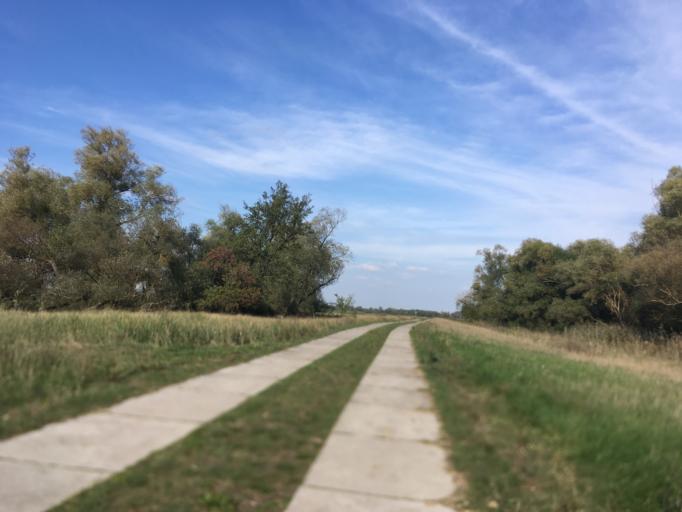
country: DE
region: Brandenburg
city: Schwedt (Oder)
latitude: 53.0234
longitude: 14.2765
